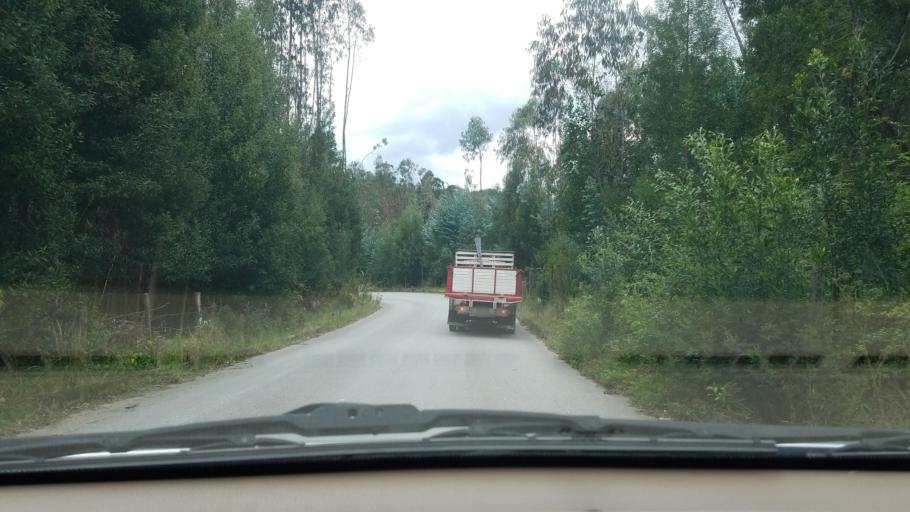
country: CO
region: Boyaca
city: Paipa
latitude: 5.7378
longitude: -73.1114
